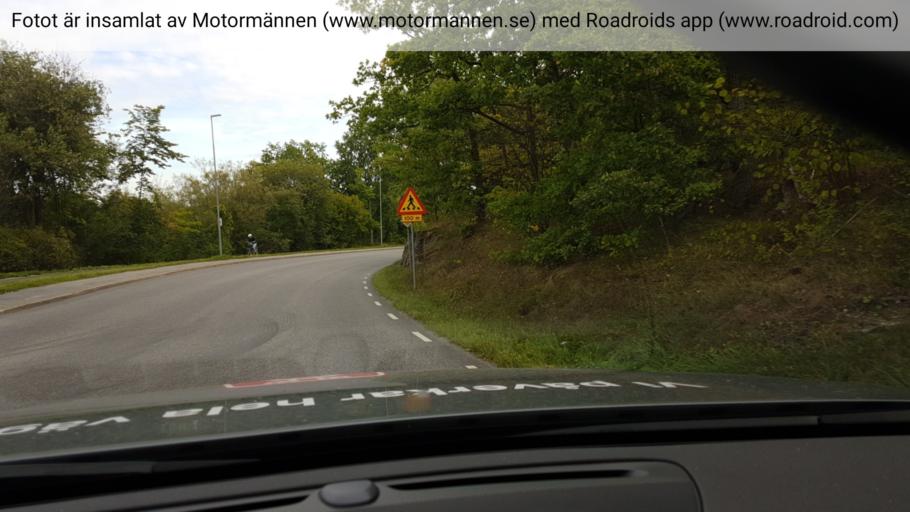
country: SE
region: Stockholm
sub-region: Danderyds Kommun
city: Djursholm
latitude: 59.3873
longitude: 18.0696
